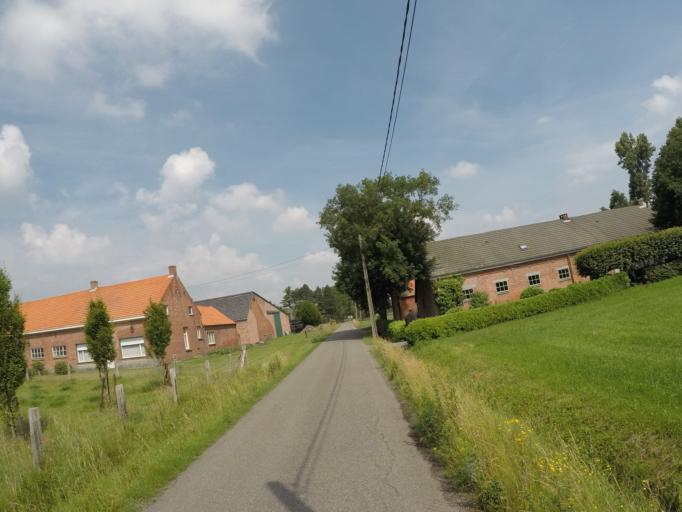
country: BE
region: Flanders
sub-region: Provincie Antwerpen
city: Brecht
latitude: 51.3433
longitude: 4.5941
